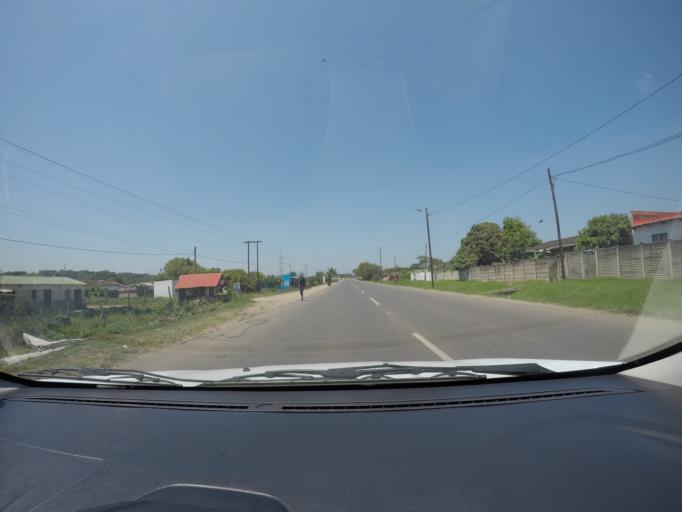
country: ZA
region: KwaZulu-Natal
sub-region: uThungulu District Municipality
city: eSikhawini
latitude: -28.8591
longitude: 31.9202
